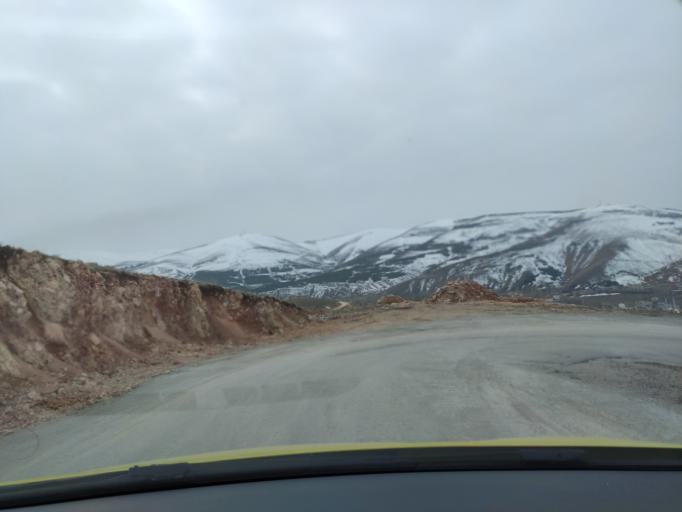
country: TR
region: Bayburt
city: Bayburt
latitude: 40.2578
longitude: 40.2381
